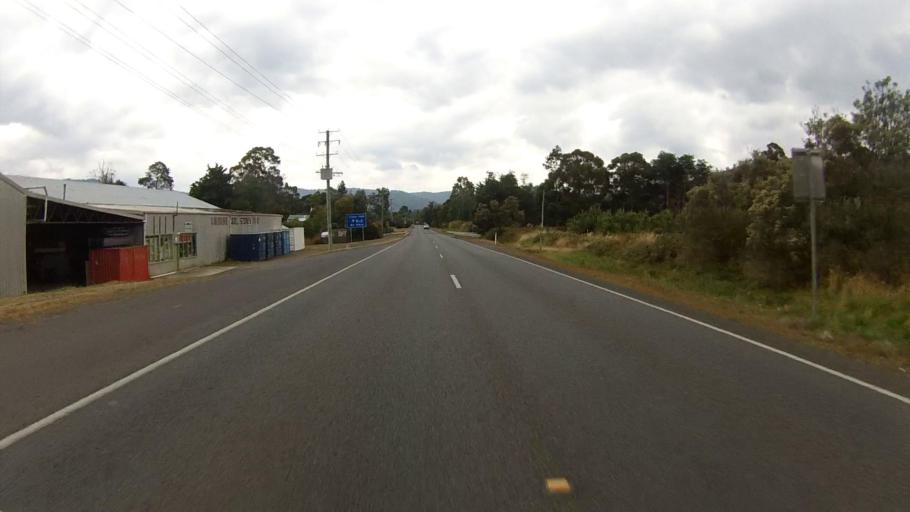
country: AU
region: Tasmania
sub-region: Huon Valley
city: Franklin
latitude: -43.1082
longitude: 147.0352
